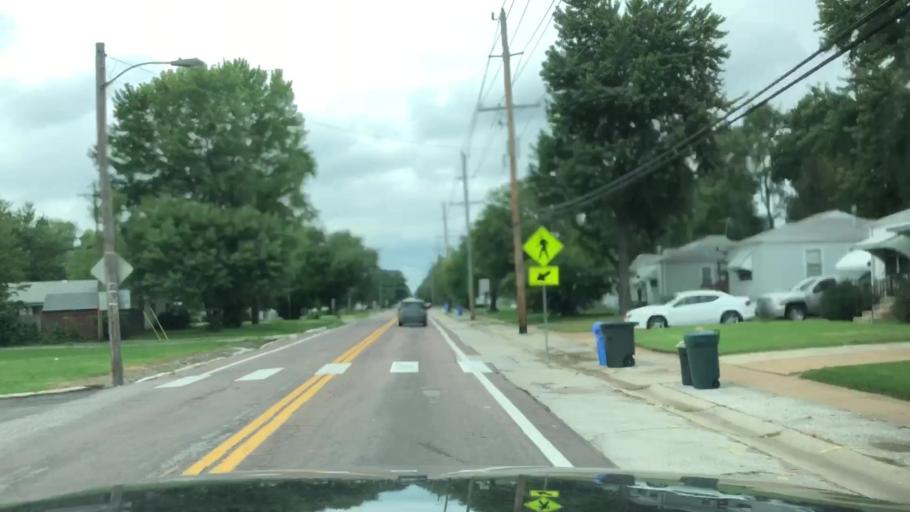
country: US
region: Missouri
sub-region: Saint Louis County
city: Florissant
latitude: 38.8000
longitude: -90.3440
